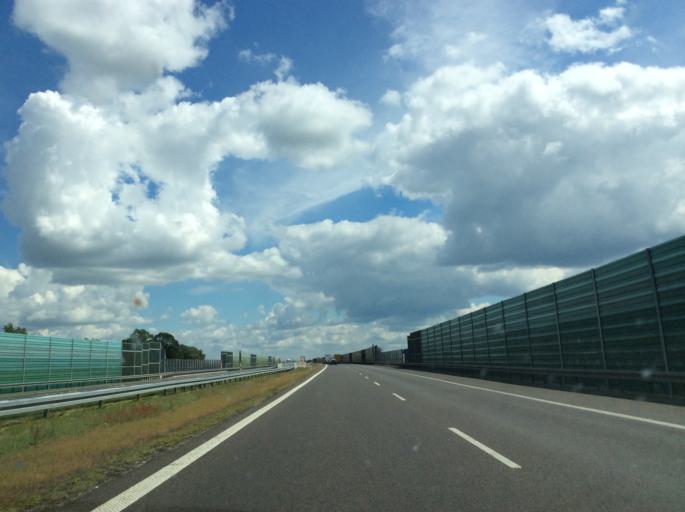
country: PL
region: Greater Poland Voivodeship
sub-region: Powiat turecki
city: Brudzew
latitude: 52.1248
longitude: 18.6772
